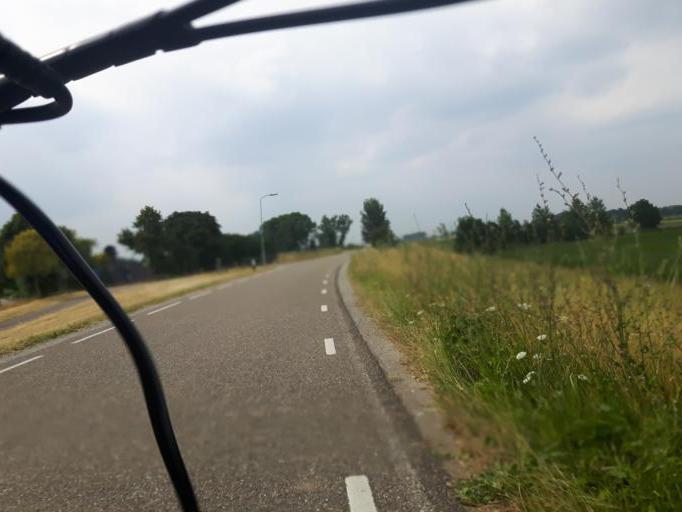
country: NL
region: North Brabant
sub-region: Gemeente Aalburg
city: Aalburg
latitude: 51.8129
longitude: 5.1163
